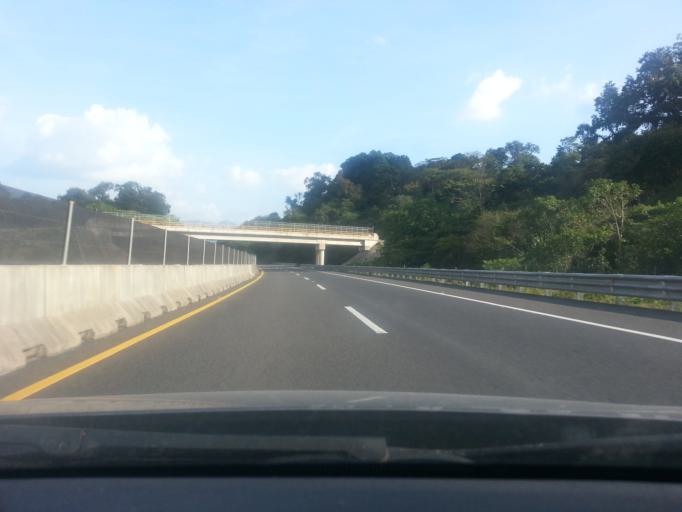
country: MX
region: Puebla
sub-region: Xicotepec
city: San Lorenzo
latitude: 20.3878
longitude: -97.9462
